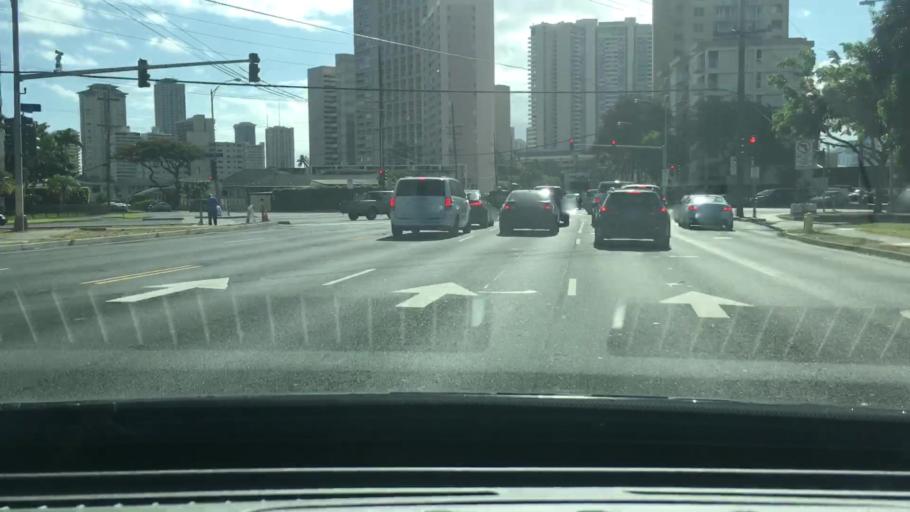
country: US
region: Hawaii
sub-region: Honolulu County
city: Honolulu
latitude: 21.2876
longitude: -157.8232
